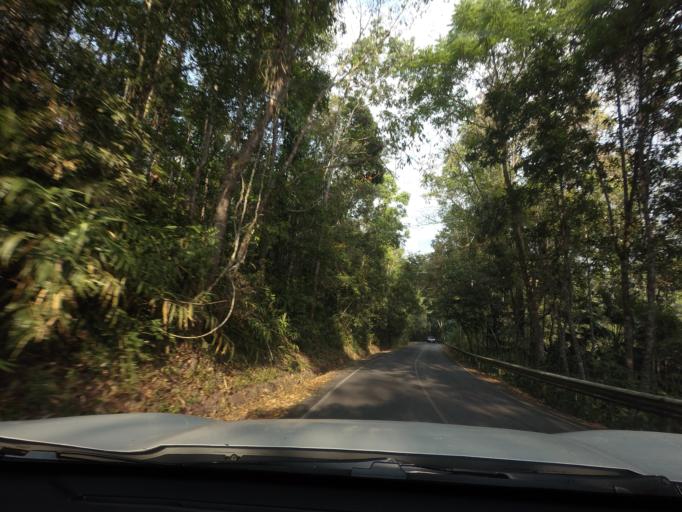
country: TH
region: Nakhon Ratchasima
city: Pak Chong
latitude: 14.4326
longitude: 101.4136
